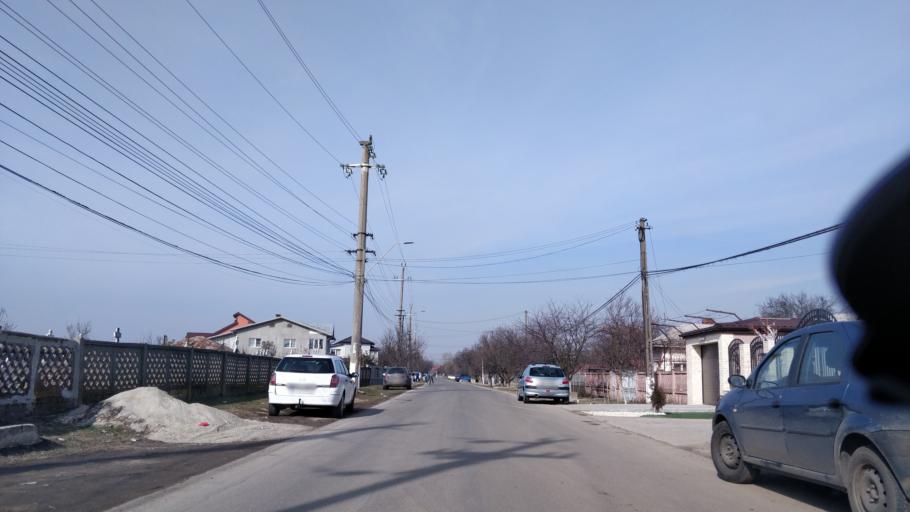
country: RO
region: Giurgiu
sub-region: Comuna Ulmi
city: Ulmi
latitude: 44.4719
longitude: 25.7667
